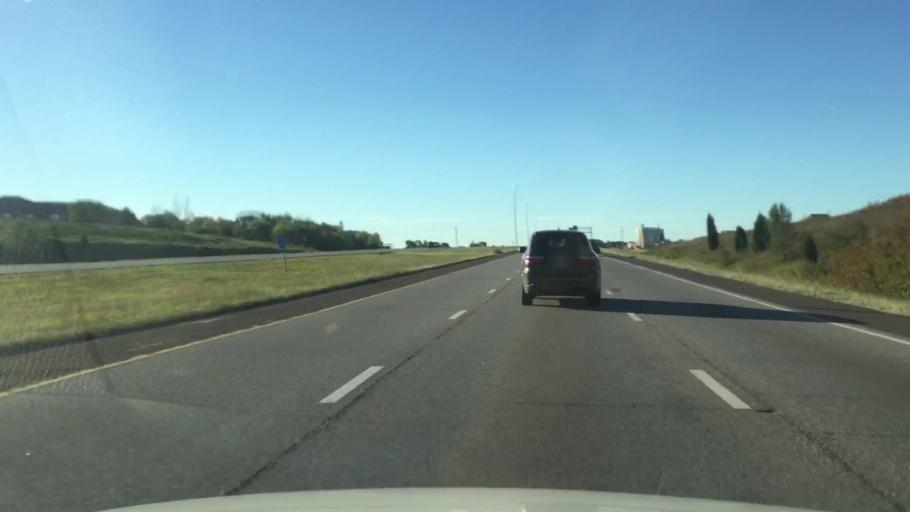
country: US
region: Kansas
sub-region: Johnson County
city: Lenexa
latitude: 38.9770
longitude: -94.7765
